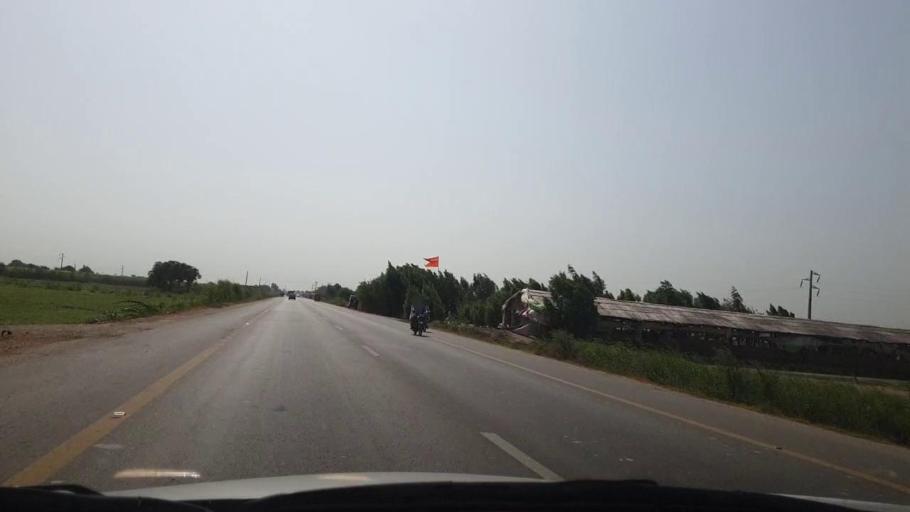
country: PK
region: Sindh
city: Tando Muhammad Khan
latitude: 25.1161
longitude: 68.5750
